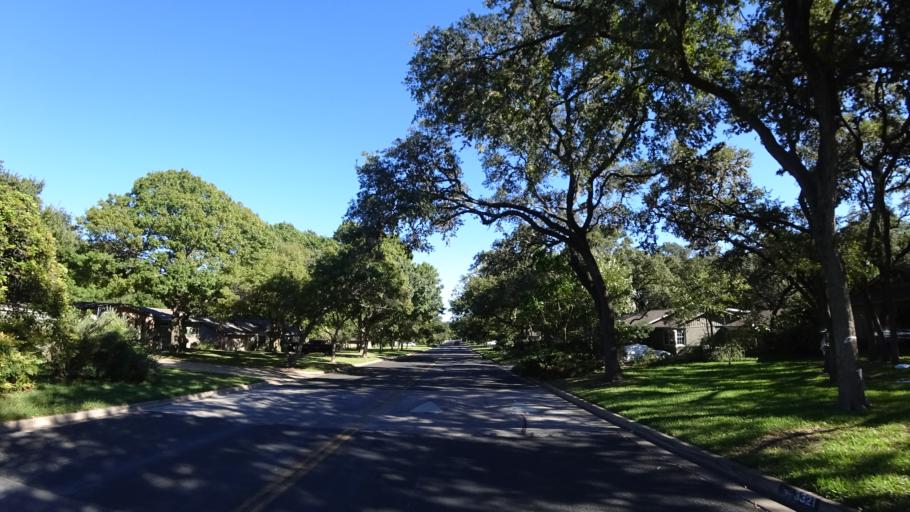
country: US
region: Texas
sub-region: Travis County
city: West Lake Hills
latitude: 30.3289
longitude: -97.7633
